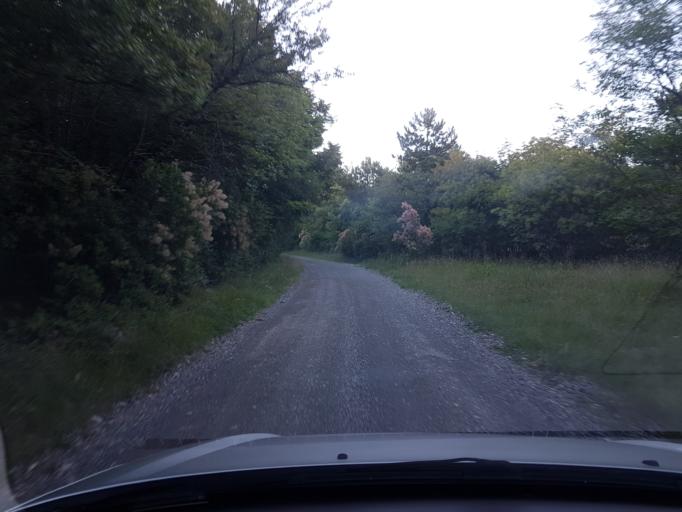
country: SI
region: Sezana
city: Sezana
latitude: 45.7224
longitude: 13.9099
